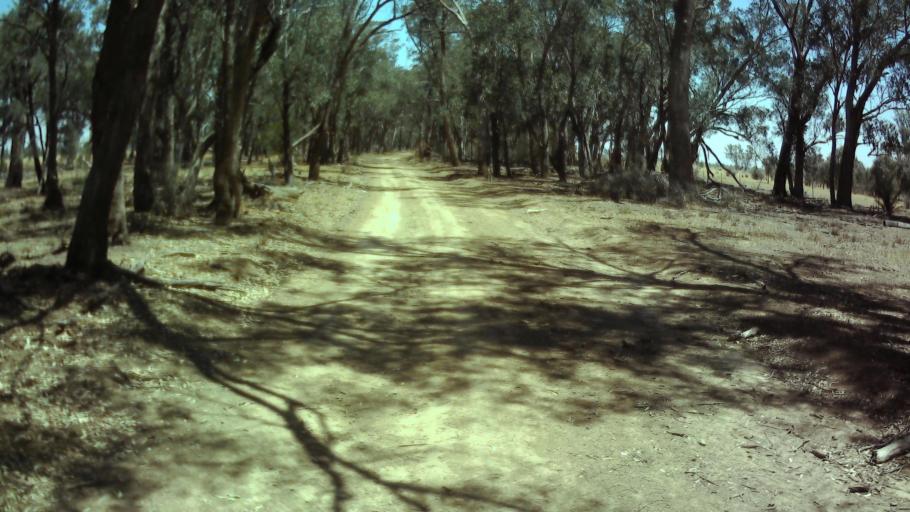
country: AU
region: New South Wales
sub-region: Weddin
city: Grenfell
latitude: -34.0475
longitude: 147.8343
